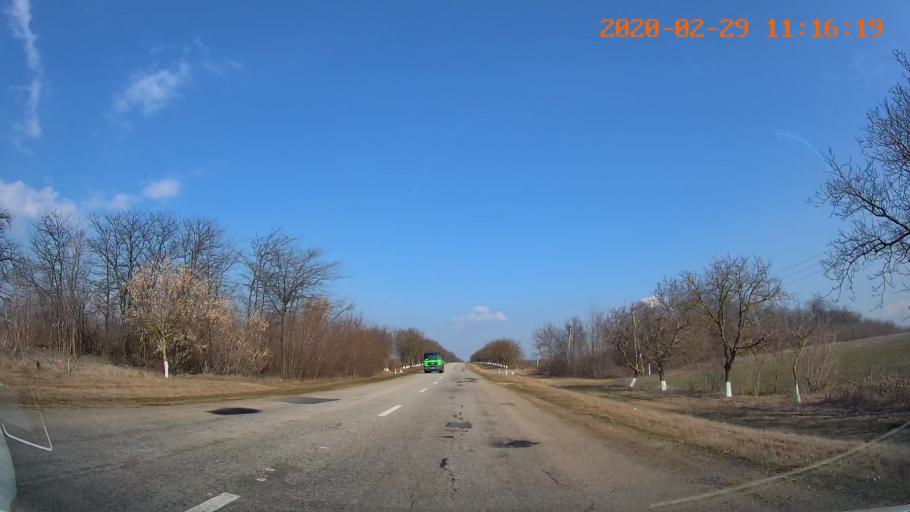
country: MD
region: Telenesti
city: Dubasari
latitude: 47.3069
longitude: 29.1675
